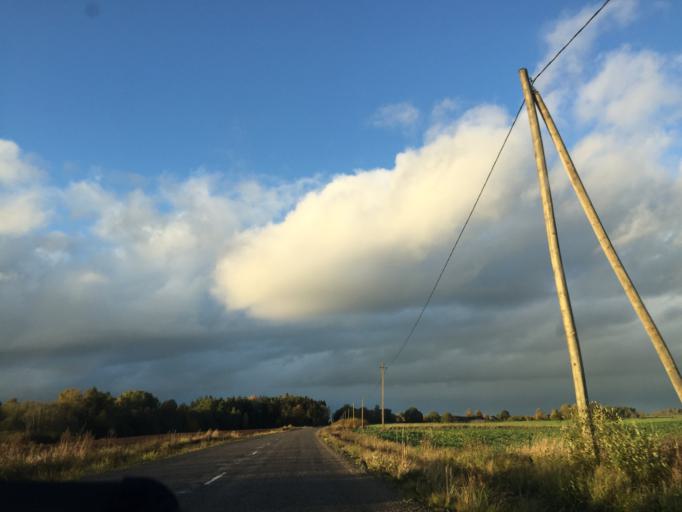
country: LV
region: Talsu Rajons
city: Sabile
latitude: 56.9007
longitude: 22.4008
